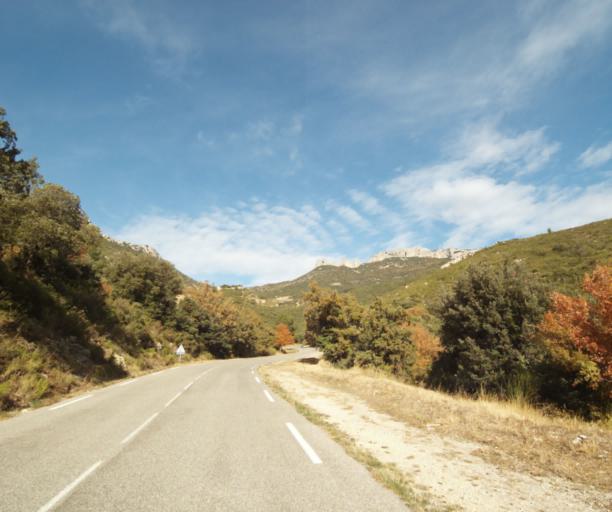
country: FR
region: Provence-Alpes-Cote d'Azur
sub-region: Departement des Bouches-du-Rhone
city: Gemenos
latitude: 43.3041
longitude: 5.6686
